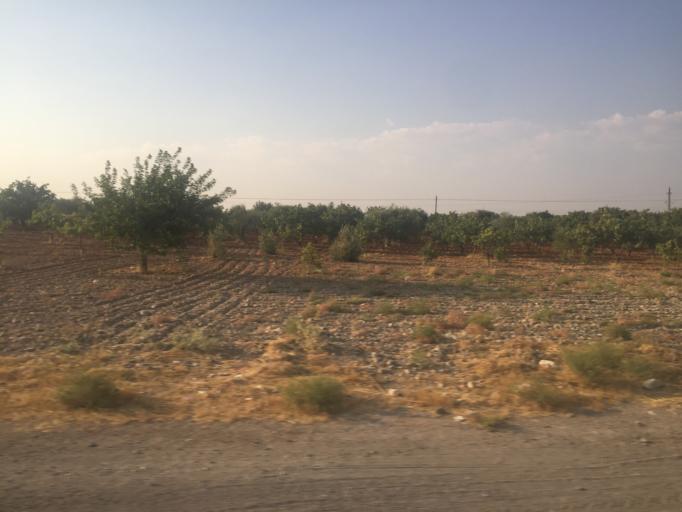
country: TR
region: Gaziantep
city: Nizip
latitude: 37.0155
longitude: 37.8831
